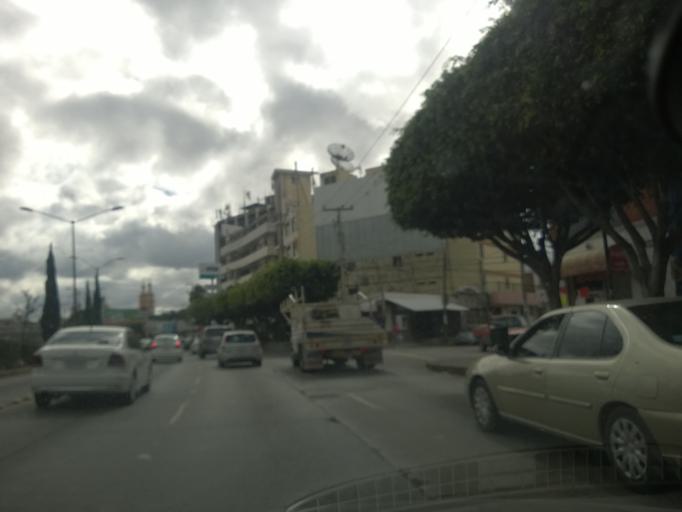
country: MX
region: Guanajuato
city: Leon
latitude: 21.1275
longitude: -101.6867
